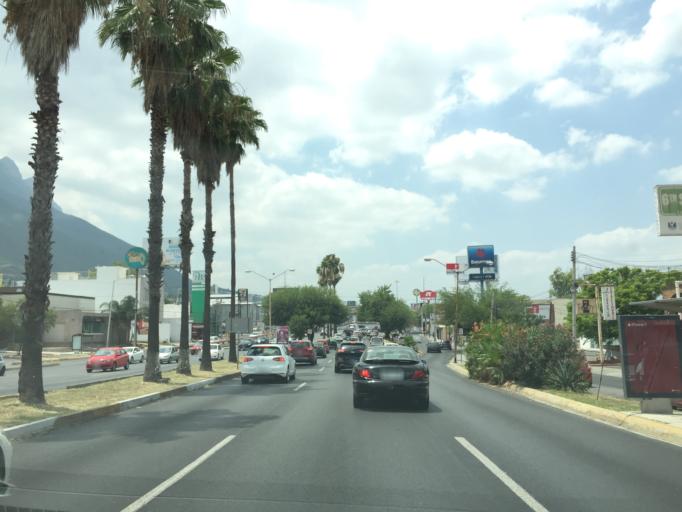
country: MX
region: Nuevo Leon
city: Garza Garcia
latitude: 25.7023
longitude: -100.3667
